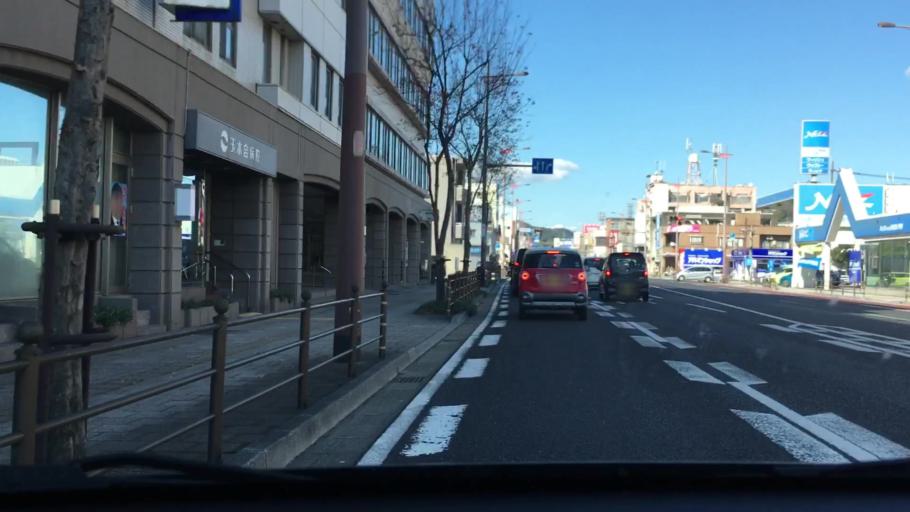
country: JP
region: Kagoshima
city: Kagoshima-shi
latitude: 31.6087
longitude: 130.5351
